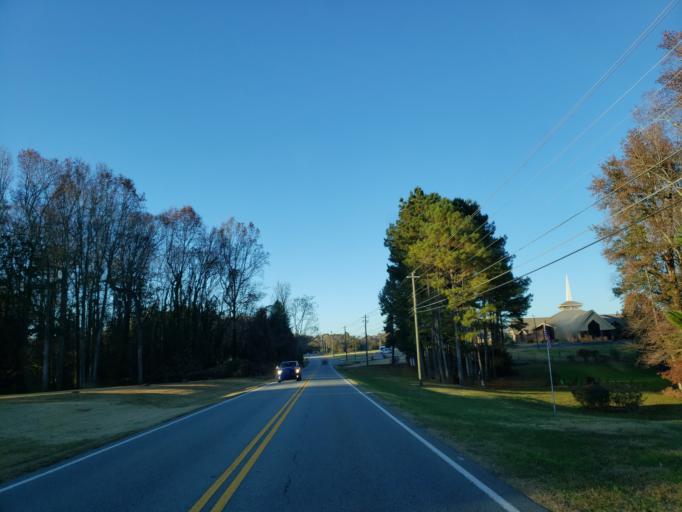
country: US
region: Georgia
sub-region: Cherokee County
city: Holly Springs
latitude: 34.1826
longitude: -84.4206
